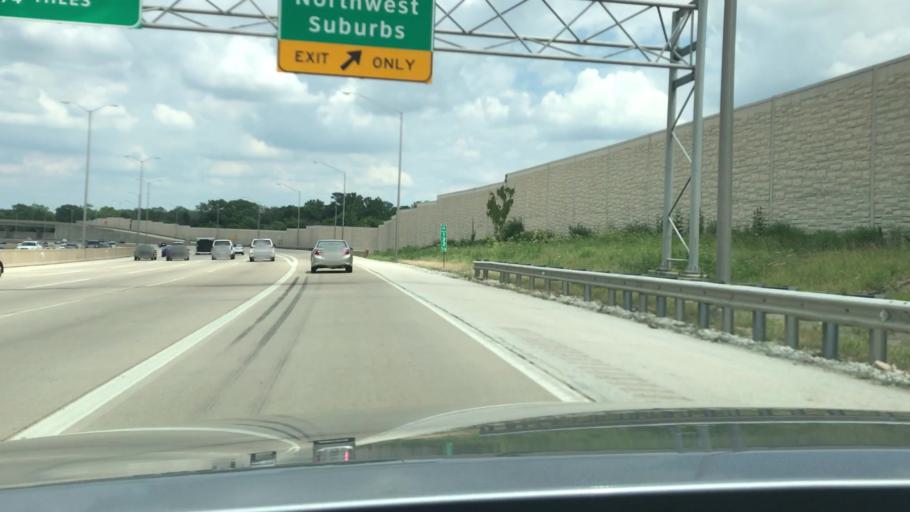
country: US
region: Illinois
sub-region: DuPage County
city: Downers Grove
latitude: 41.8094
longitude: -88.0362
